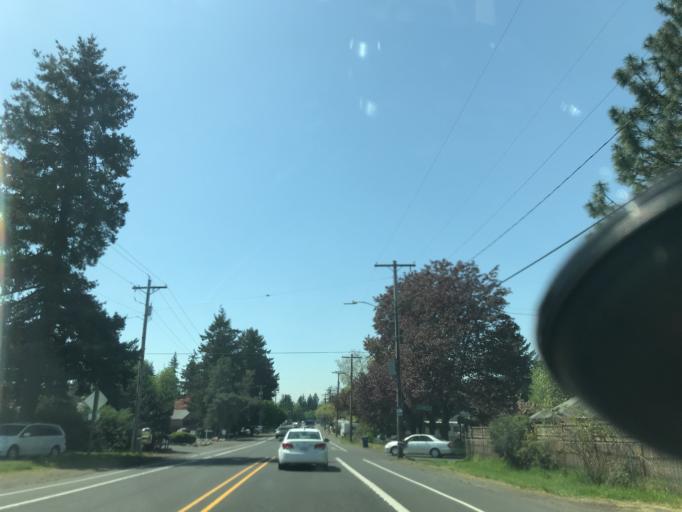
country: US
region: Oregon
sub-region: Multnomah County
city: Lents
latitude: 45.4987
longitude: -122.5189
